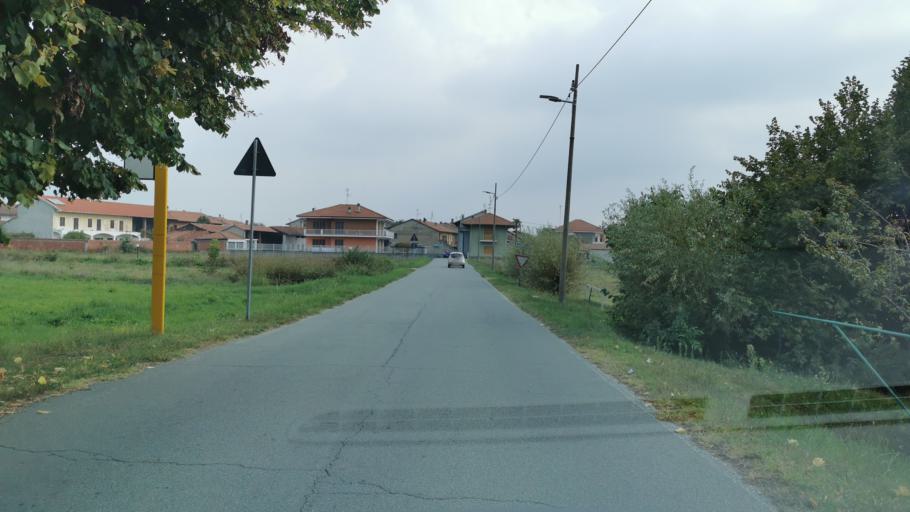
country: IT
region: Piedmont
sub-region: Provincia di Torino
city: Tonengo-Casale
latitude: 45.2891
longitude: 7.9417
